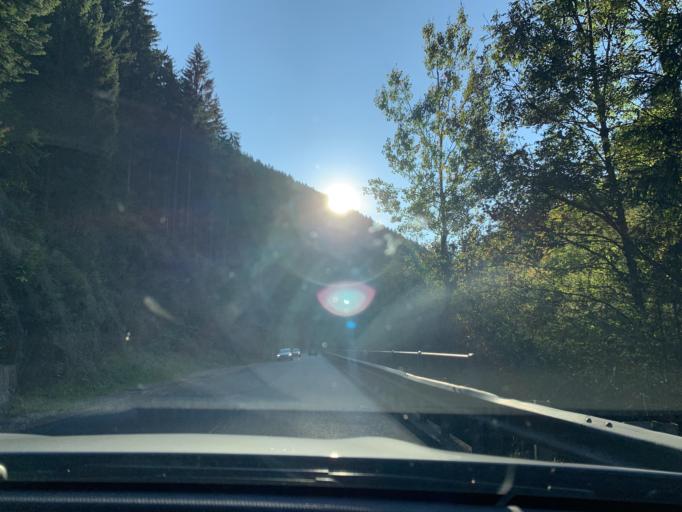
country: IT
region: Trentino-Alto Adige
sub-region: Bolzano
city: Nova Levante
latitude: 46.4263
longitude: 11.5195
